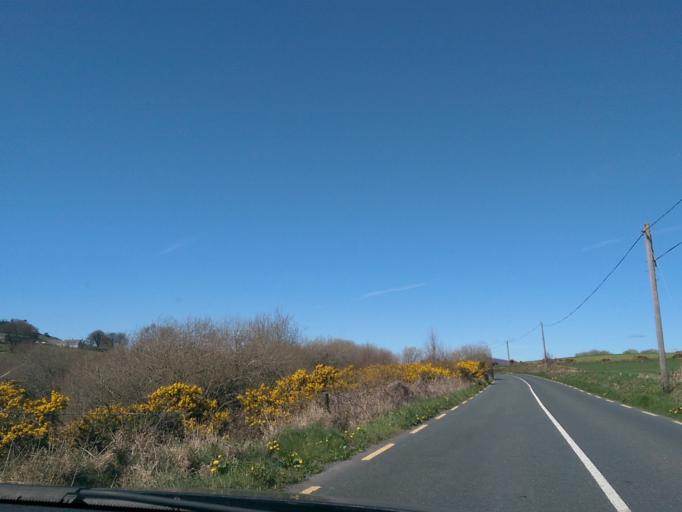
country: IE
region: Leinster
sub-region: Wicklow
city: Carnew
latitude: 52.8503
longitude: -6.5464
